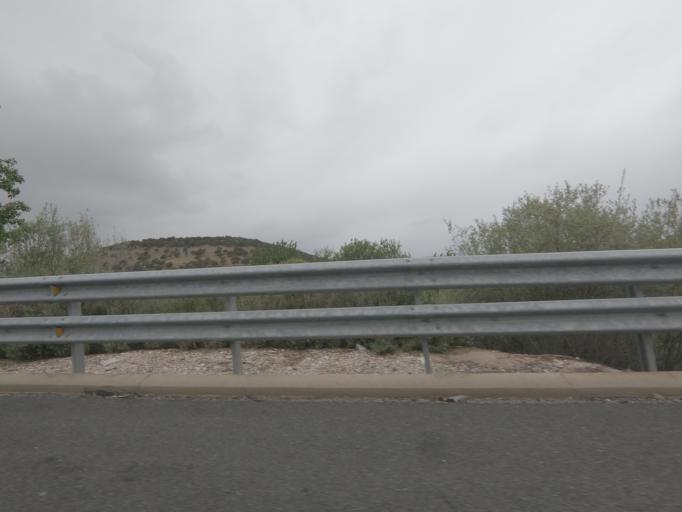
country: ES
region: Extremadura
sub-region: Provincia de Caceres
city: Villar de Plasencia
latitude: 40.1616
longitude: -6.0259
